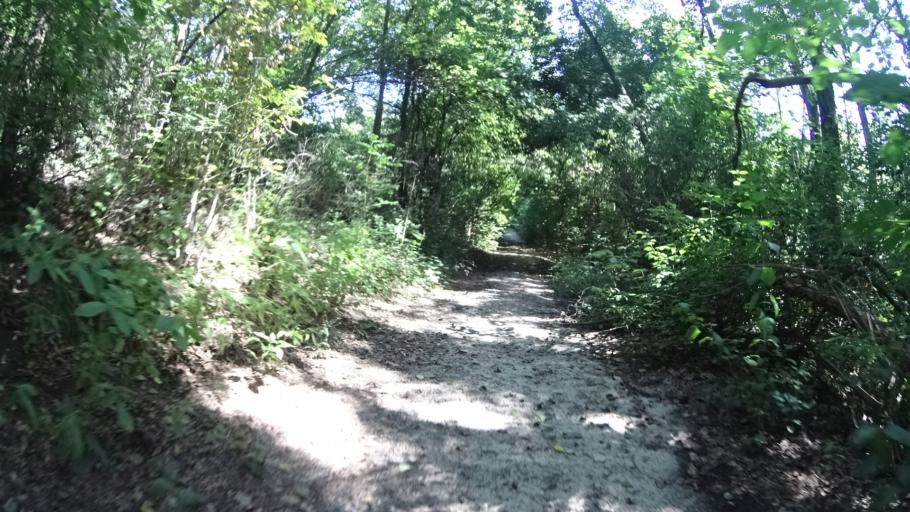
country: PL
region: Masovian Voivodeship
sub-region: Powiat bialobrzeski
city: Bialobrzegi
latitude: 51.6673
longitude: 20.9050
